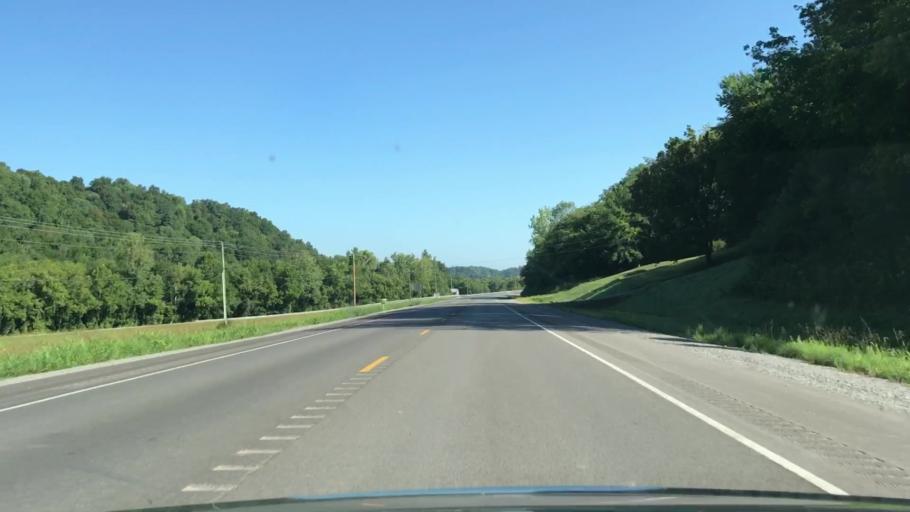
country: US
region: Kentucky
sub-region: Cumberland County
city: Burkesville
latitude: 36.7380
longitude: -85.3732
